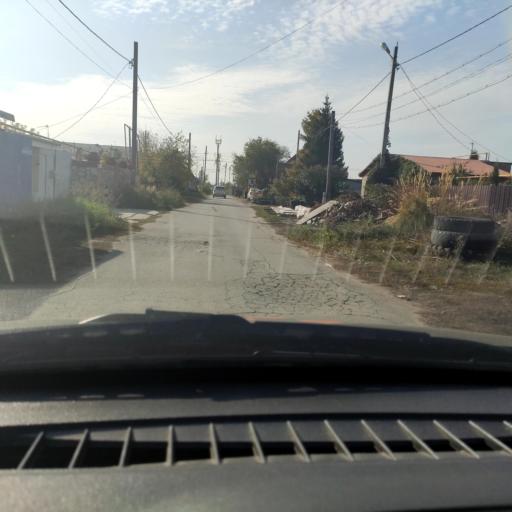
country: RU
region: Samara
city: Podstepki
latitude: 53.5135
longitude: 49.2310
